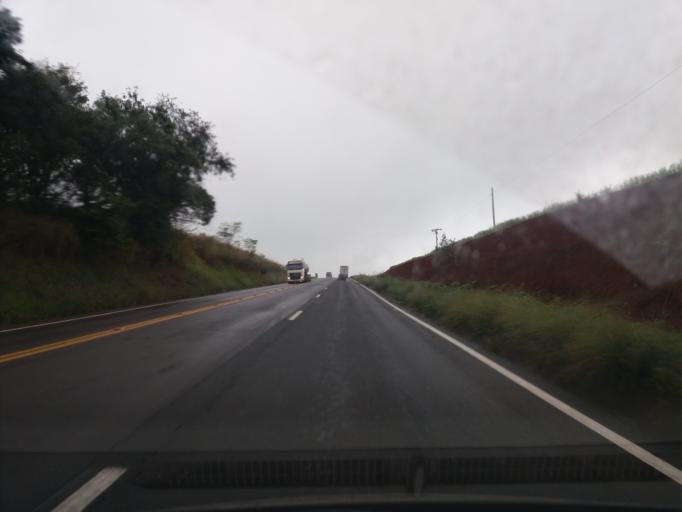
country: BR
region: Parana
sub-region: Realeza
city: Realeza
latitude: -25.5568
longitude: -53.5851
